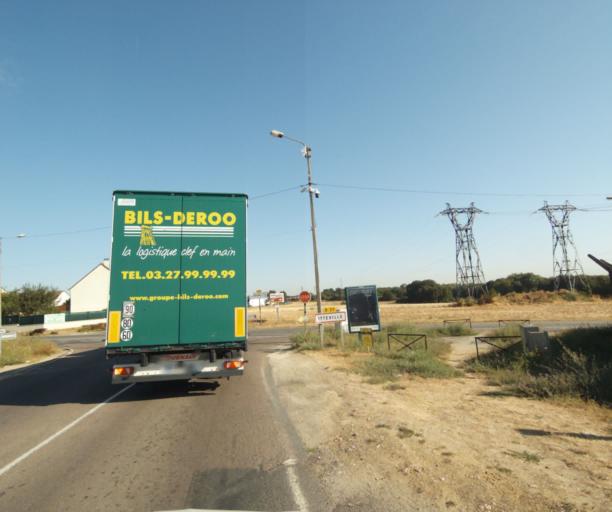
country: FR
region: Ile-de-France
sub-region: Departement de l'Essonne
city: Itteville
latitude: 48.5208
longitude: 2.3548
